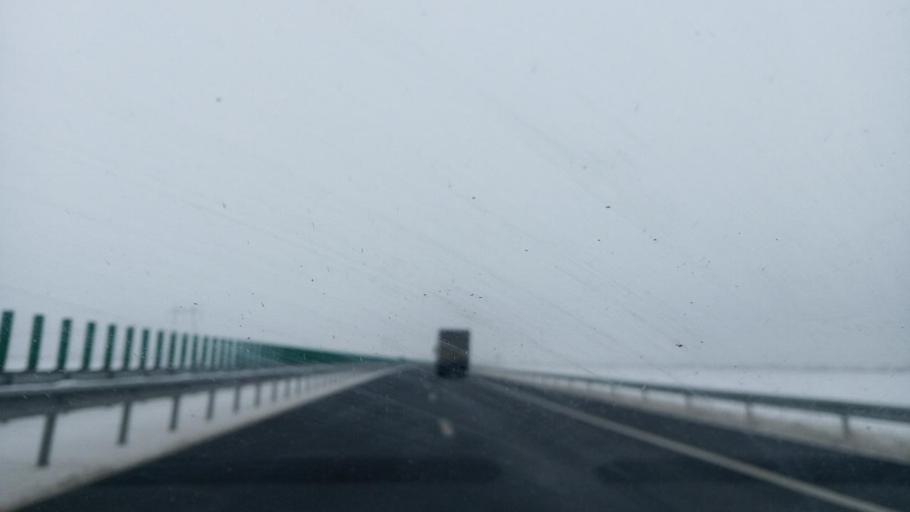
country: RO
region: Bacau
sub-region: Comuna Letea Veche
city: Holt
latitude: 46.5683
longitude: 26.9656
